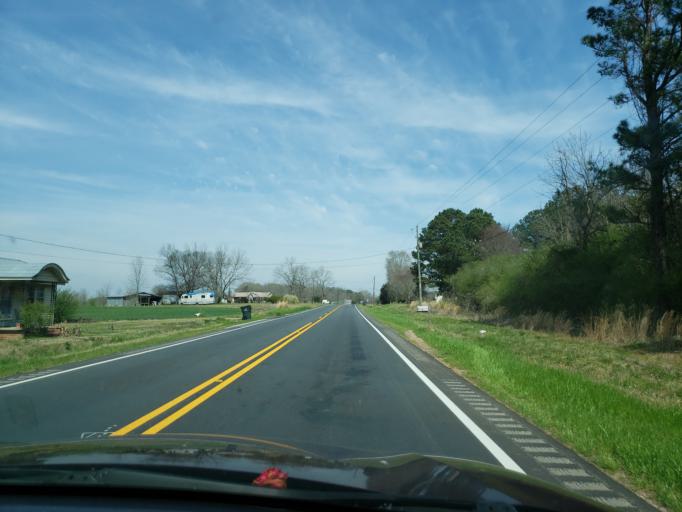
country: US
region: Alabama
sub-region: Elmore County
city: Tallassee
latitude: 32.5662
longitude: -85.7773
